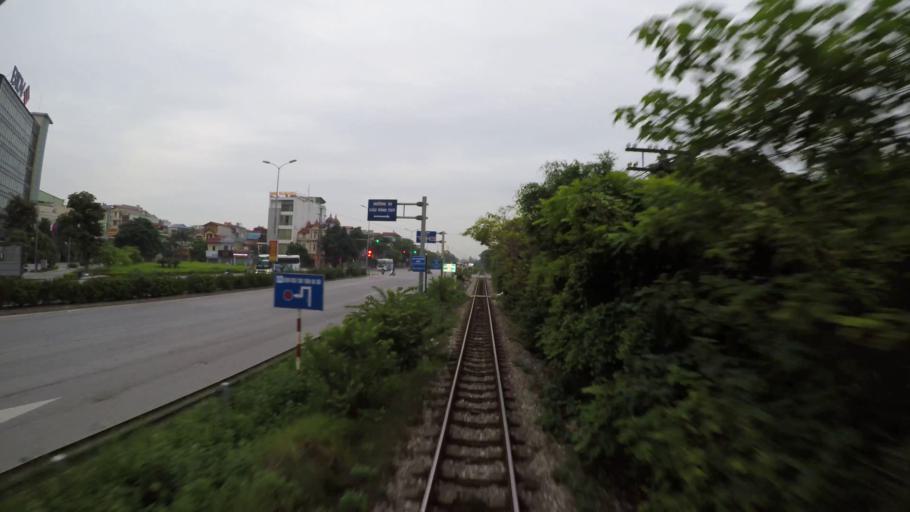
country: VN
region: Ha Noi
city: Trau Quy
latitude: 21.0042
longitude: 105.9614
